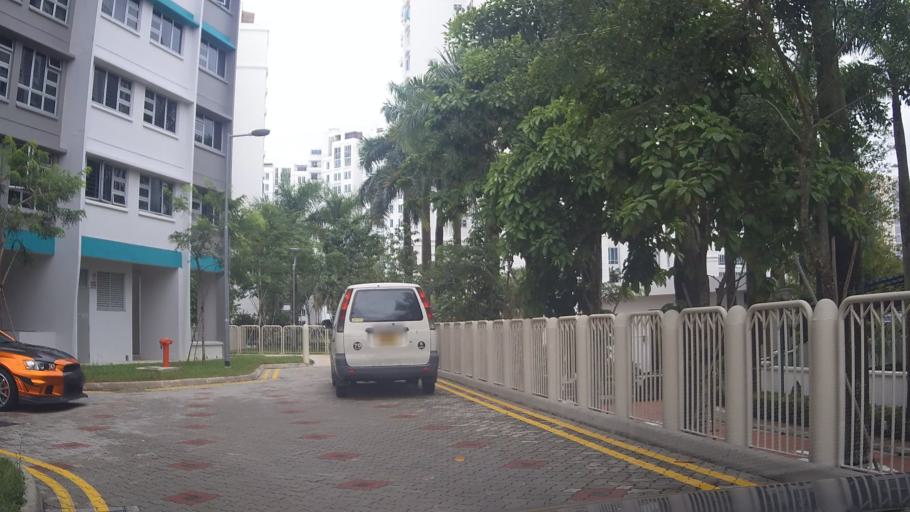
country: MY
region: Johor
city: Johor Bahru
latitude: 1.4452
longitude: 103.8052
